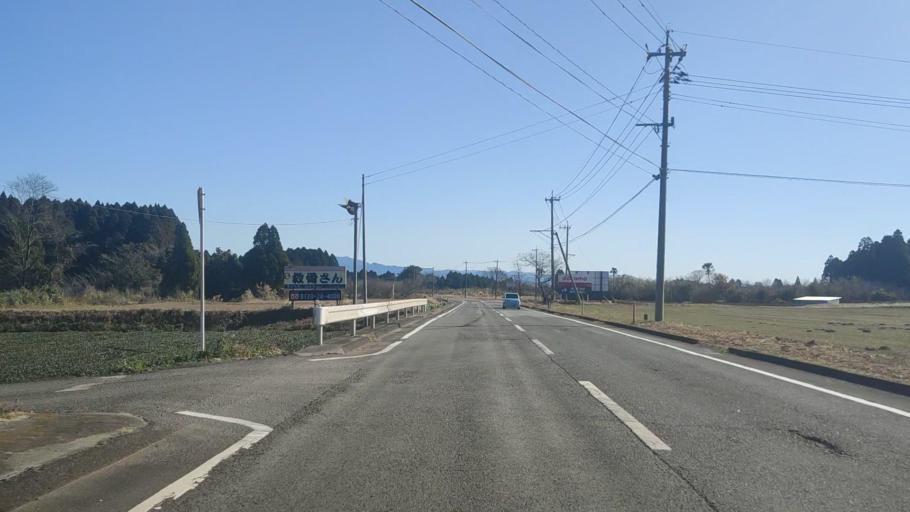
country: JP
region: Kagoshima
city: Sueyoshicho-ninokata
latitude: 31.6877
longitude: 130.9638
